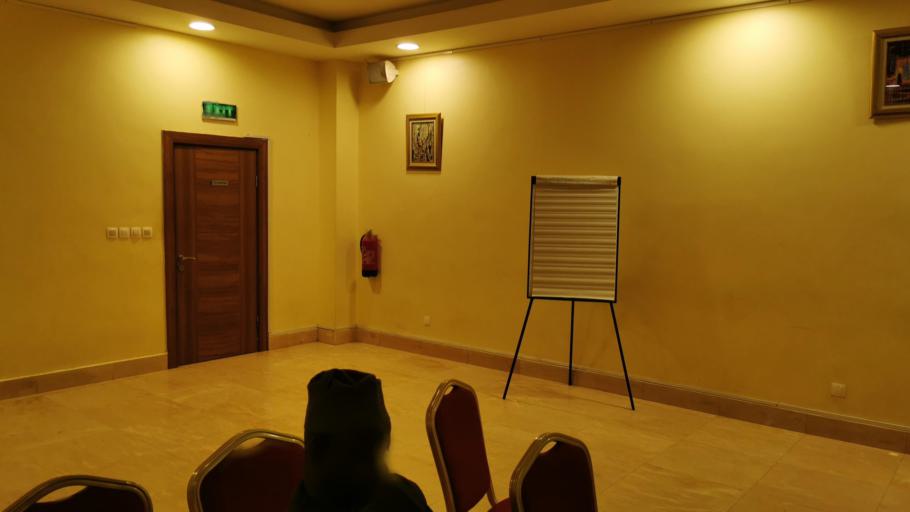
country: ML
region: Bamako
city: Bamako
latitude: 12.6332
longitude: -8.0158
